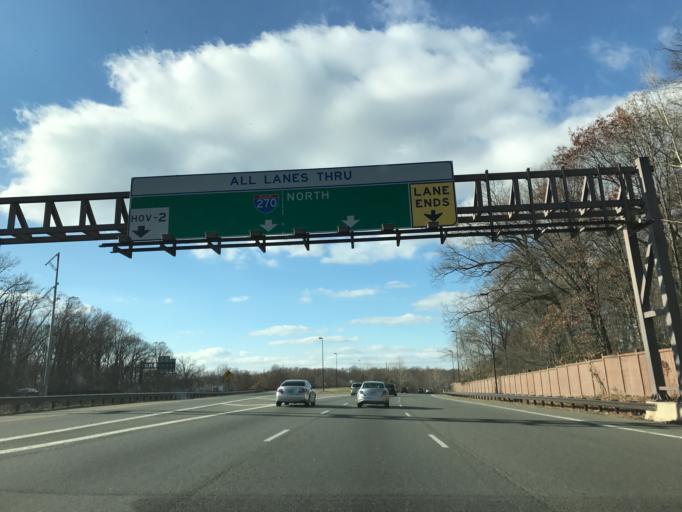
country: US
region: Maryland
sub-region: Montgomery County
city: North Bethesda
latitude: 39.0327
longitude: -77.1381
